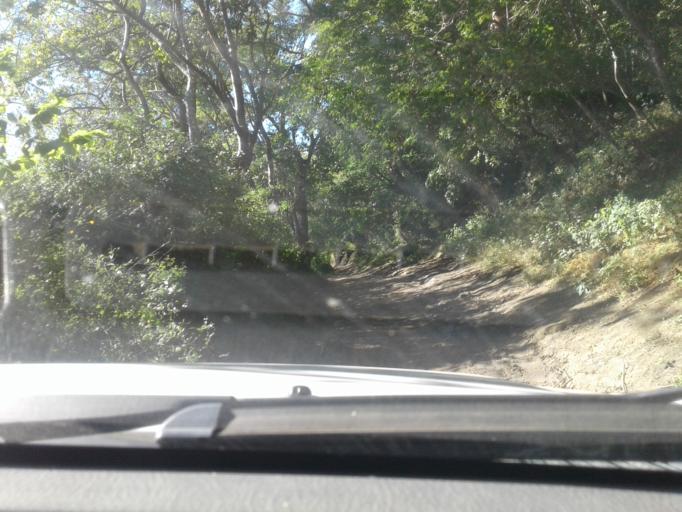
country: NI
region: Carazo
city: Santa Teresa
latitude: 11.7873
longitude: -86.1855
